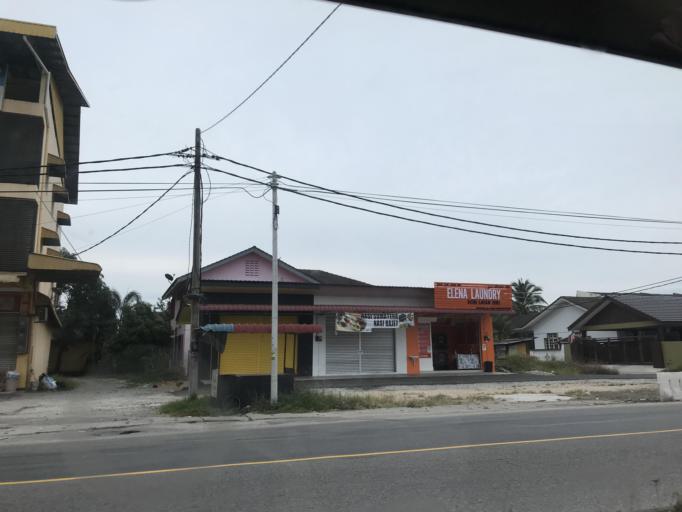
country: MY
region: Kelantan
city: Kota Bharu
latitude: 6.1206
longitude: 102.2079
